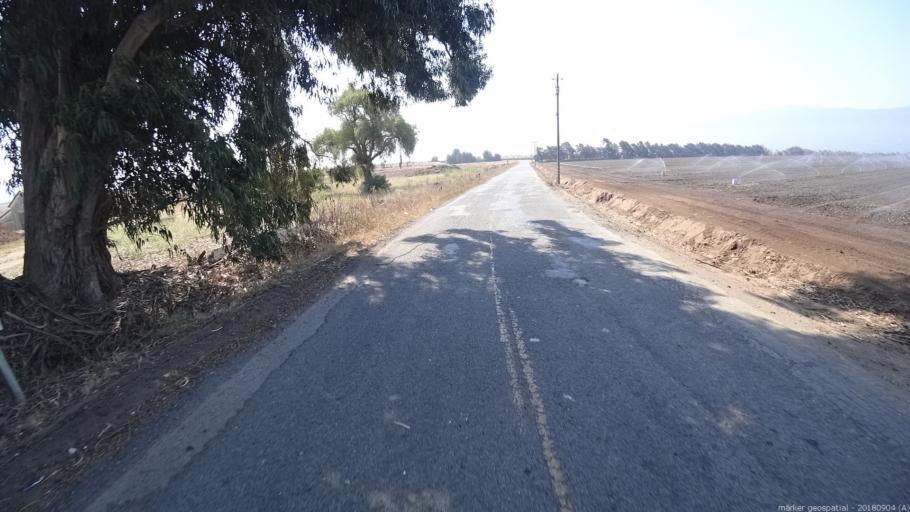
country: US
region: California
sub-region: Monterey County
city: Gonzales
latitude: 36.5180
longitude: -121.4119
